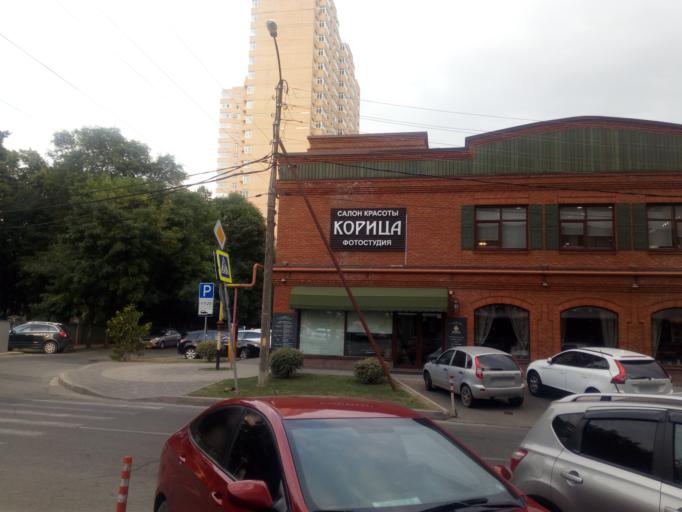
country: RU
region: Krasnodarskiy
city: Krasnodar
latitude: 45.0400
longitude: 38.9855
